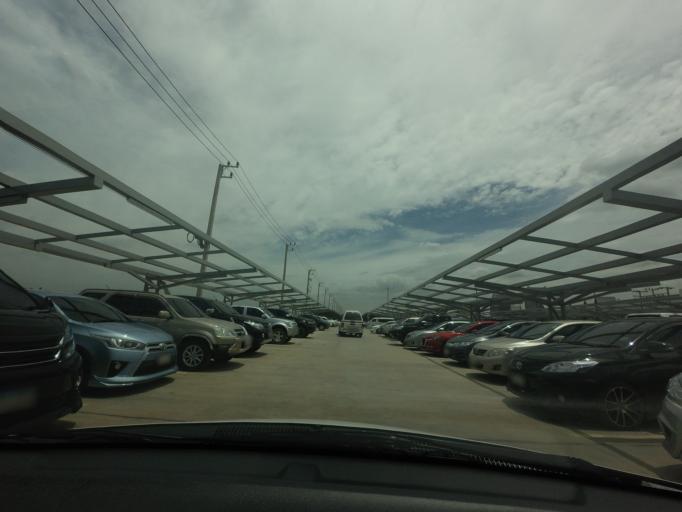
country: TH
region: Samut Prakan
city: Ban Khlong Bang Sao Thong
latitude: 13.6392
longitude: 100.7444
